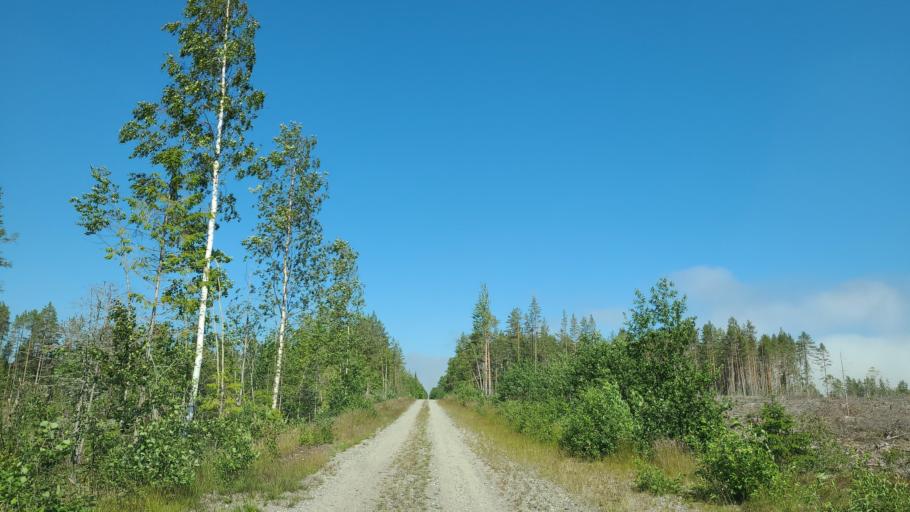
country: SE
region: Vaesternorrland
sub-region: OErnskoeldsviks Kommun
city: Husum
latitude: 63.4317
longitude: 19.2291
